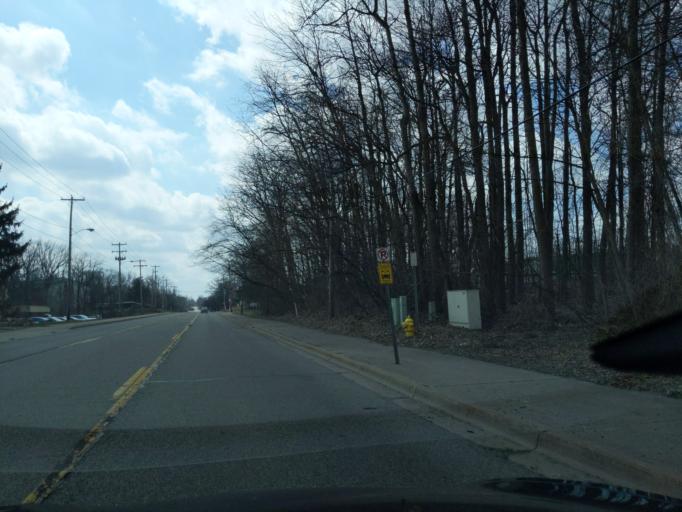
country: US
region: Michigan
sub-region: Calhoun County
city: Lakeview
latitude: 42.2545
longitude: -85.1987
